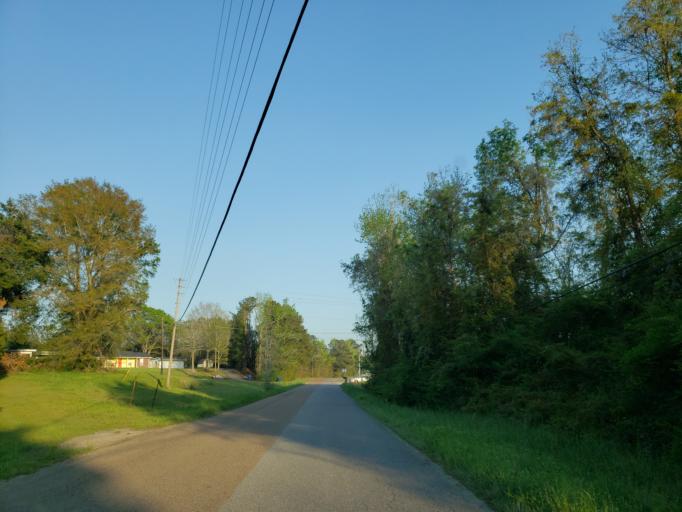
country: US
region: Mississippi
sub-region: Lauderdale County
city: Marion
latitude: 32.3981
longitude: -88.5842
